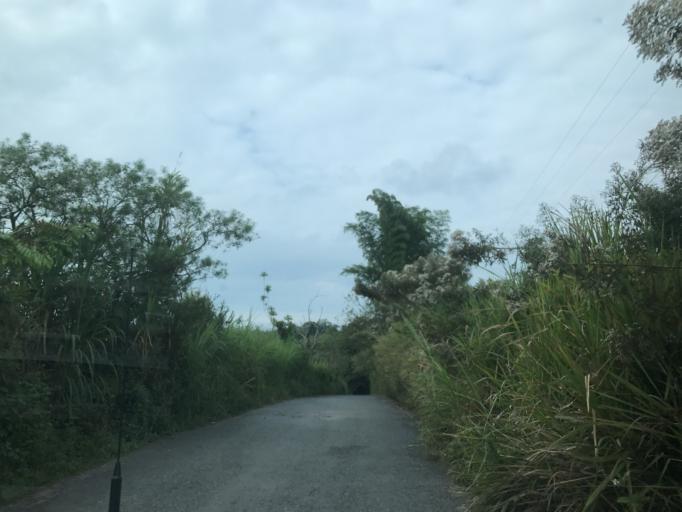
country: CO
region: Quindio
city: Montenegro
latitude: 4.5506
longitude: -75.7989
